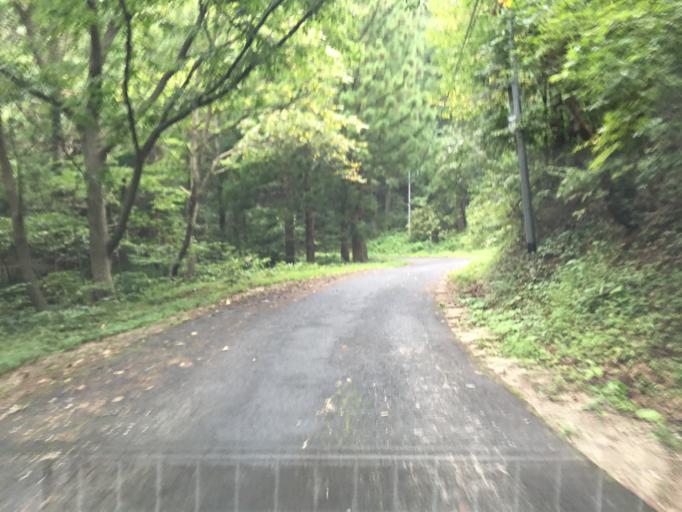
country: JP
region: Fukushima
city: Fukushima-shi
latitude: 37.8118
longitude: 140.3504
